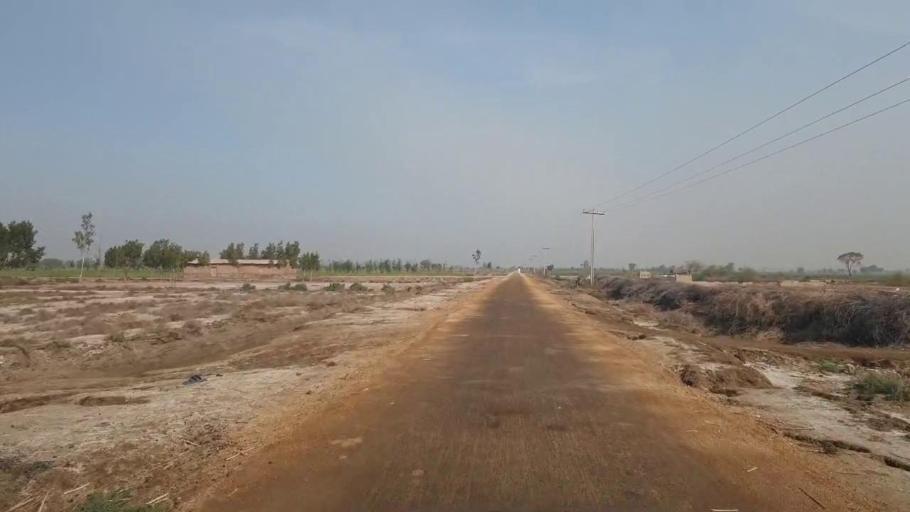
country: PK
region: Sindh
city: Mirwah Gorchani
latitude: 25.3684
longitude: 69.1665
